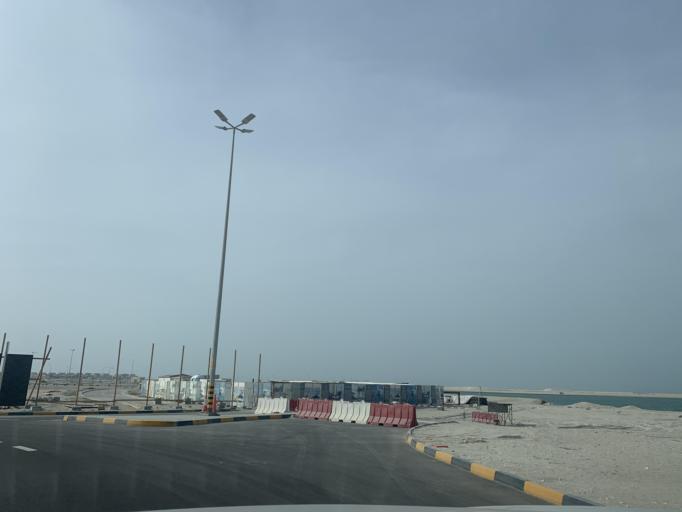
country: BH
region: Muharraq
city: Al Muharraq
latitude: 26.3149
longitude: 50.6348
